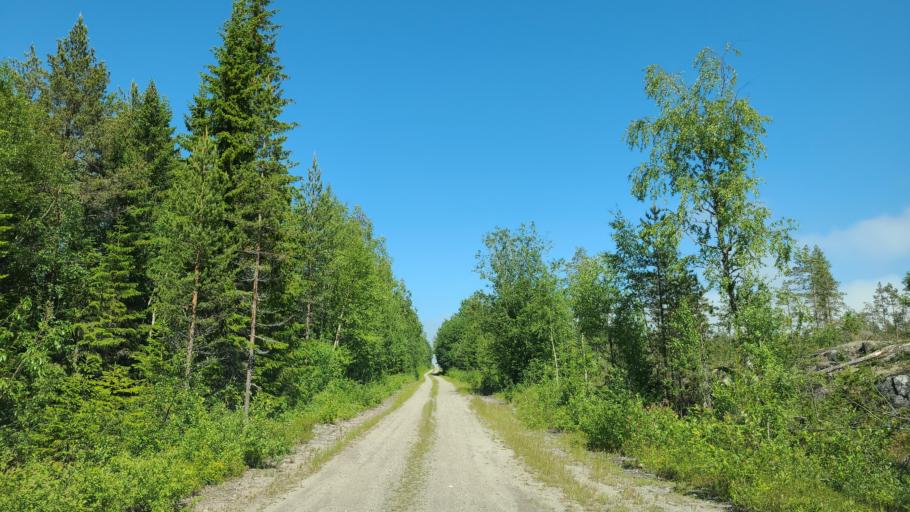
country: SE
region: Vaesternorrland
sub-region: OErnskoeldsviks Kommun
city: Husum
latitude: 63.4343
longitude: 19.2304
